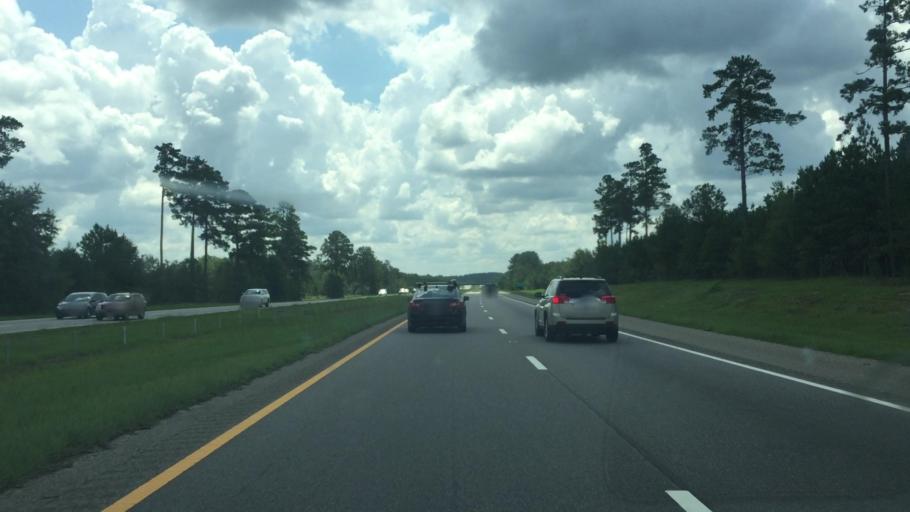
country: US
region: North Carolina
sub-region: Richmond County
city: East Rockingham
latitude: 34.8669
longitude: -79.7530
